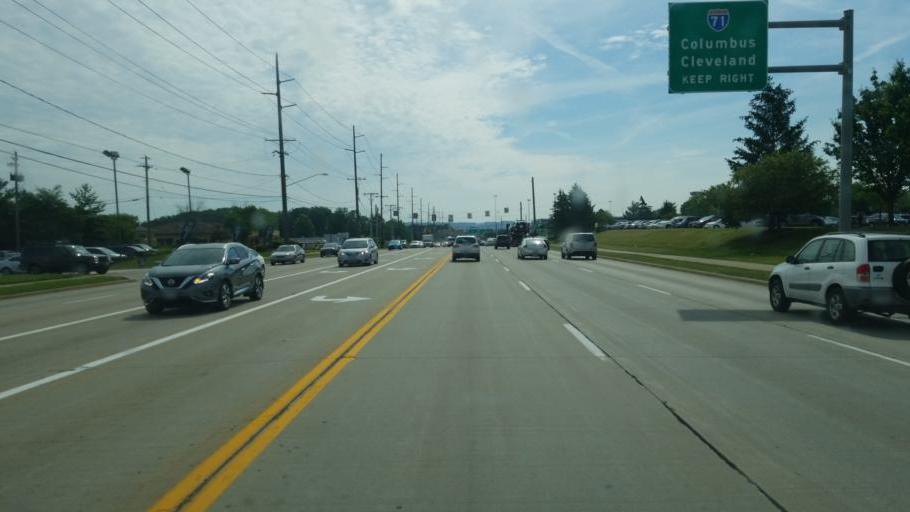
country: US
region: Ohio
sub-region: Cuyahoga County
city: Strongsville
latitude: 41.3130
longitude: -81.8193
